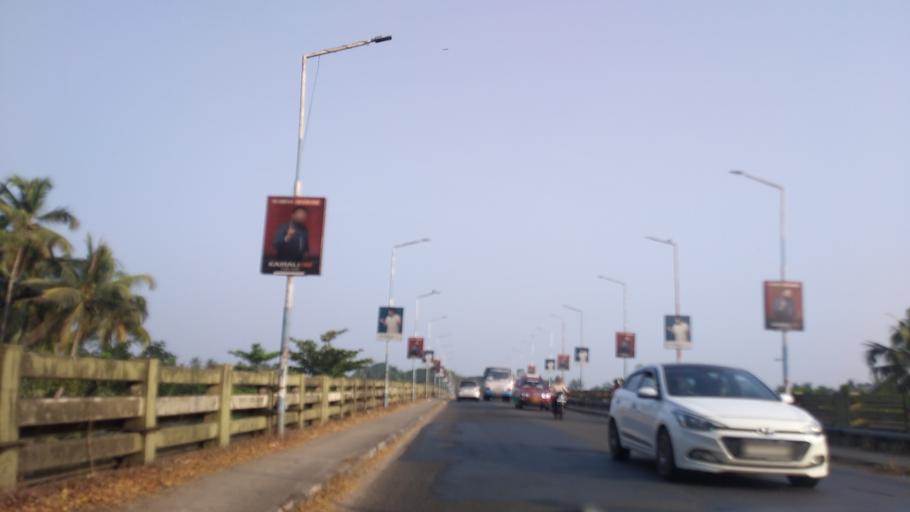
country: IN
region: Kerala
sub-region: Thrissur District
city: Kodungallur
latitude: 10.1982
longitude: 76.2007
